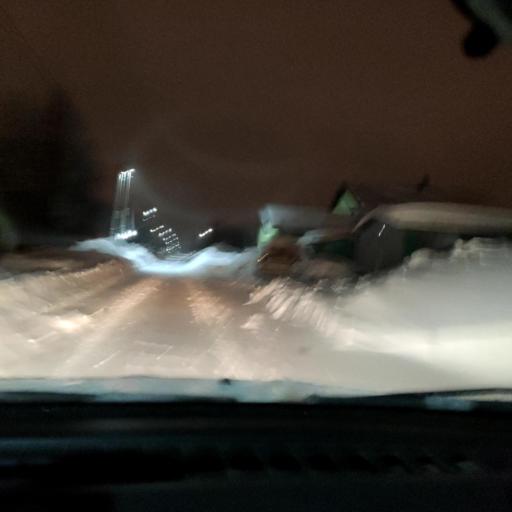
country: RU
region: Bashkortostan
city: Iglino
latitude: 54.7798
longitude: 56.2455
